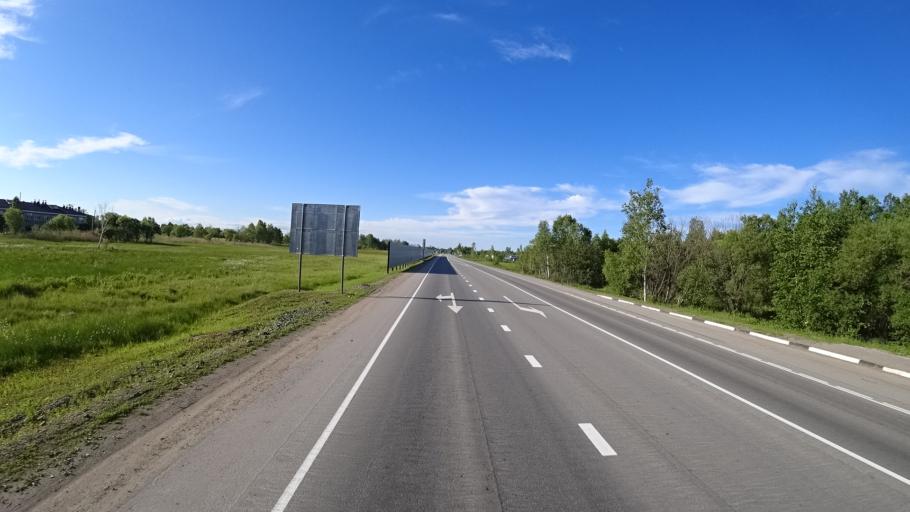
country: RU
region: Khabarovsk Krai
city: Khor
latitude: 47.8468
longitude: 134.9585
